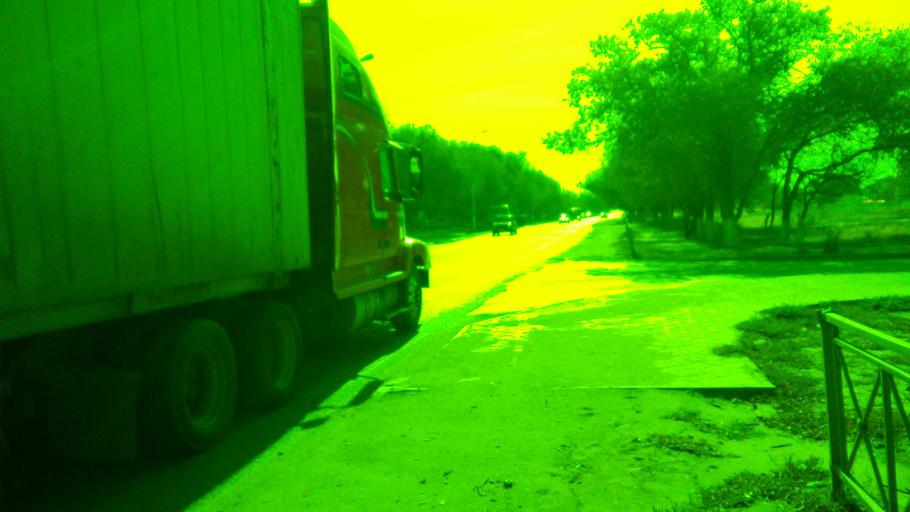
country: RU
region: Volgograd
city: Vodstroy
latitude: 48.8387
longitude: 44.6464
